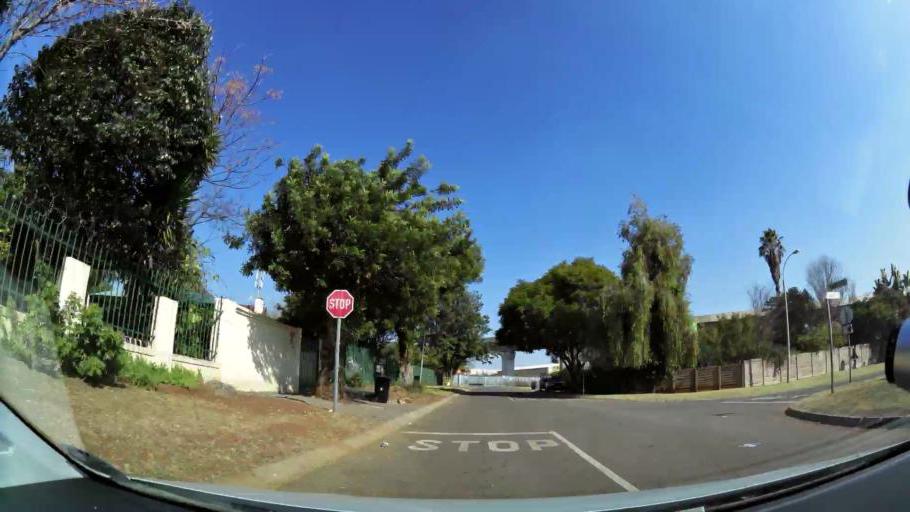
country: ZA
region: Gauteng
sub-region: City of Johannesburg Metropolitan Municipality
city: Modderfontein
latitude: -26.1245
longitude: 28.2243
